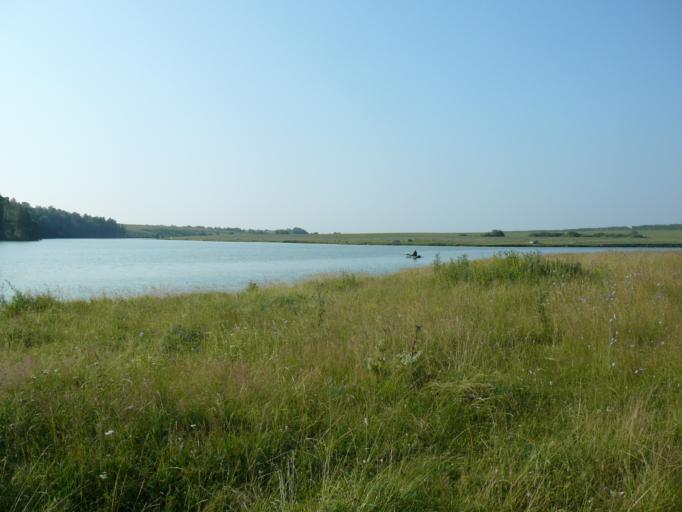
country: RU
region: Penza
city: Kondol'
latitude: 52.5974
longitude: 45.1683
